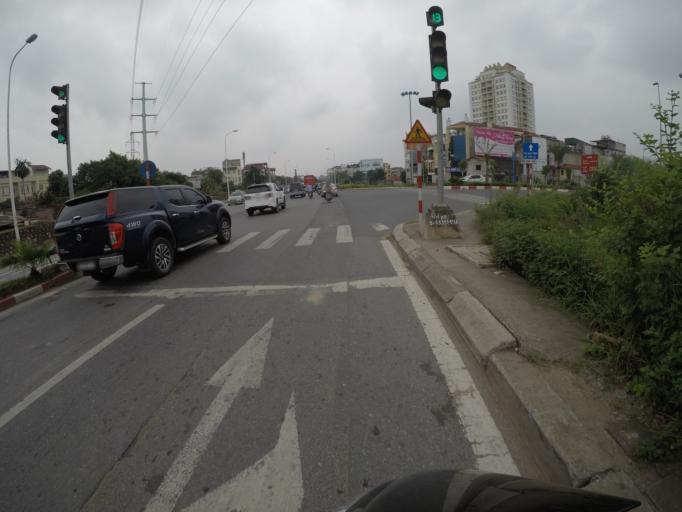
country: VN
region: Ha Noi
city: Tay Ho
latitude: 21.0826
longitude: 105.8172
